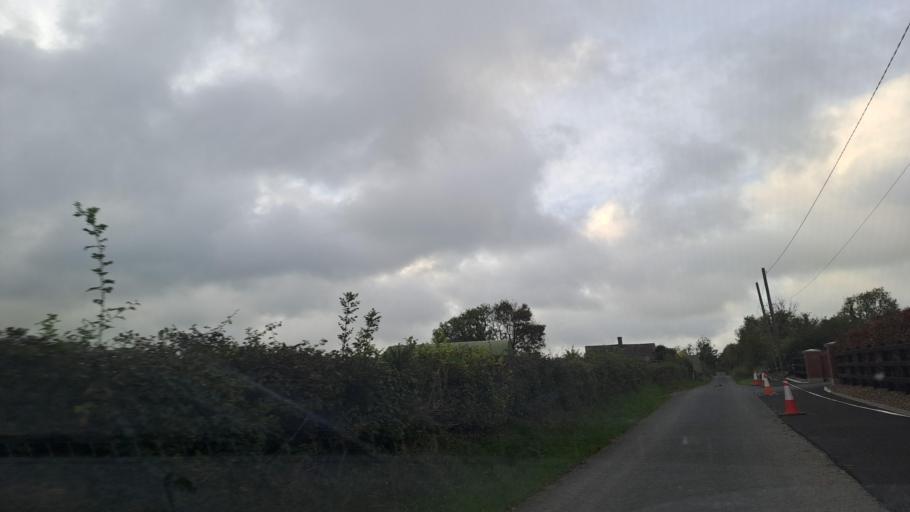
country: IE
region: Ulster
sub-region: County Monaghan
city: Carrickmacross
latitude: 54.0160
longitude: -6.7577
